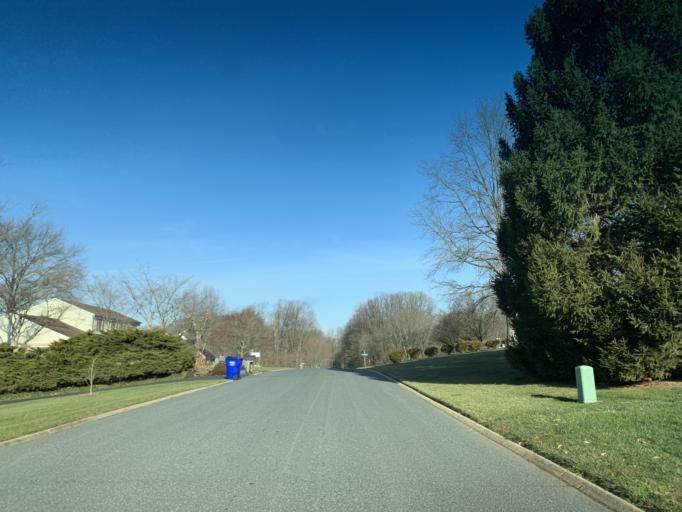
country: US
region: Maryland
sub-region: Harford County
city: South Bel Air
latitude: 39.5668
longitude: -76.2668
